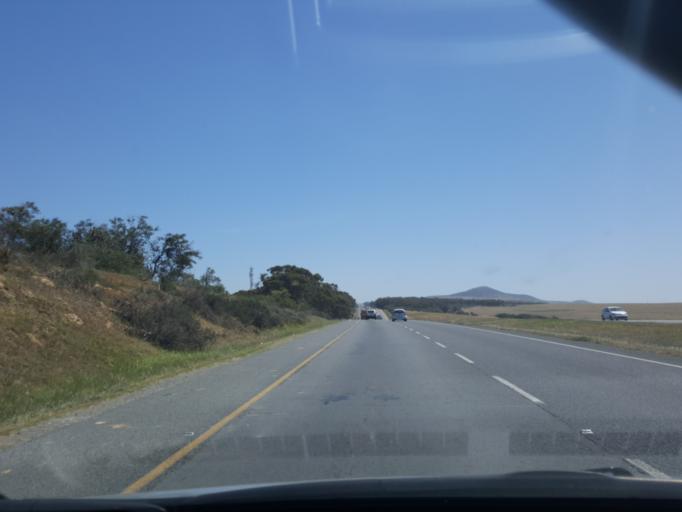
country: ZA
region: Western Cape
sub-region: City of Cape Town
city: Sunset Beach
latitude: -33.7844
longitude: 18.5490
